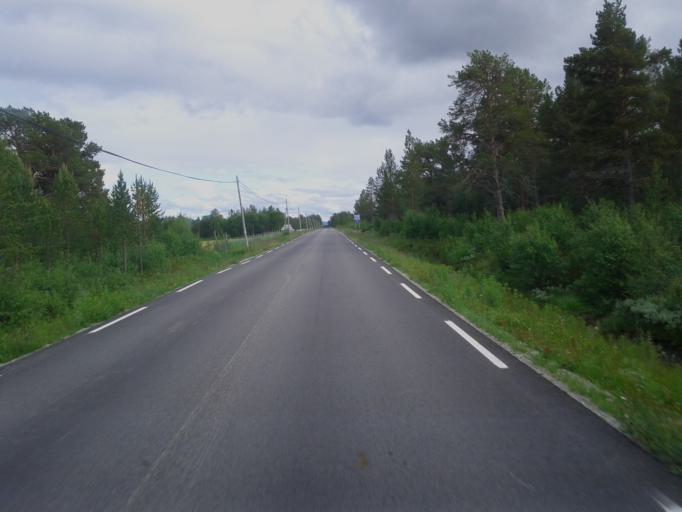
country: NO
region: Sor-Trondelag
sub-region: Roros
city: Roros
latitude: 62.2951
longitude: 11.7272
